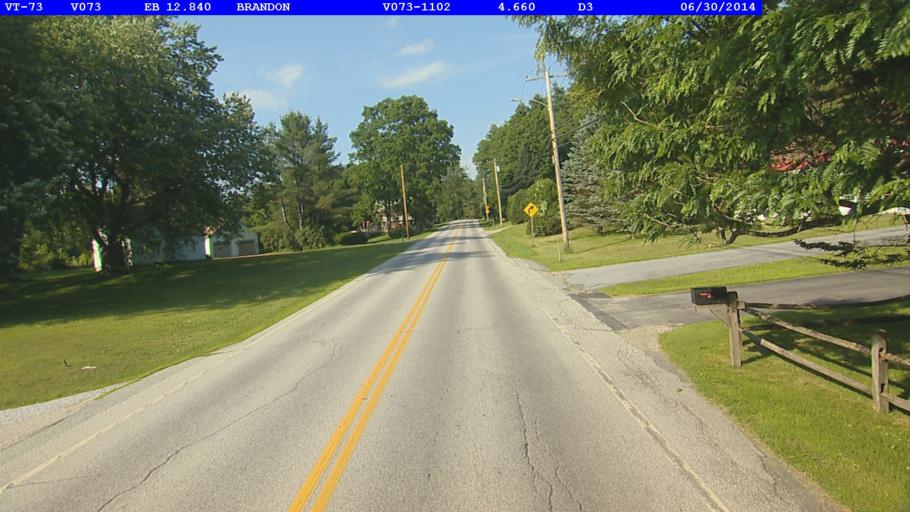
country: US
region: Vermont
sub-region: Rutland County
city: Brandon
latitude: 43.8145
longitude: -73.0698
